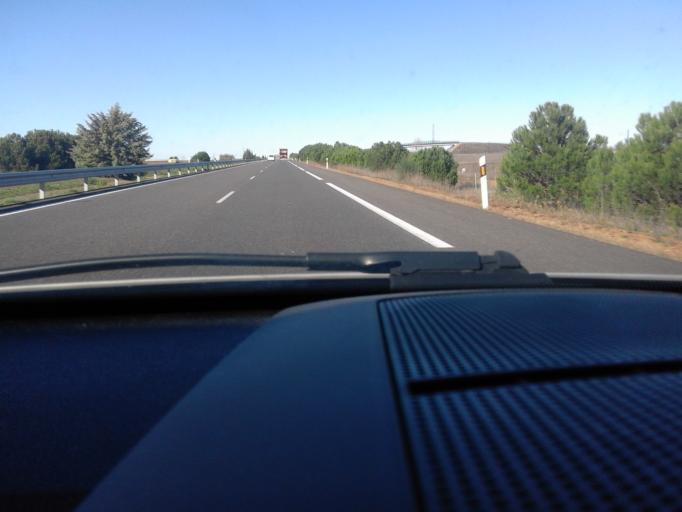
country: ES
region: Castille and Leon
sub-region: Provincia de Leon
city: Bercianos del Real Camino
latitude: 42.4058
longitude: -5.1789
